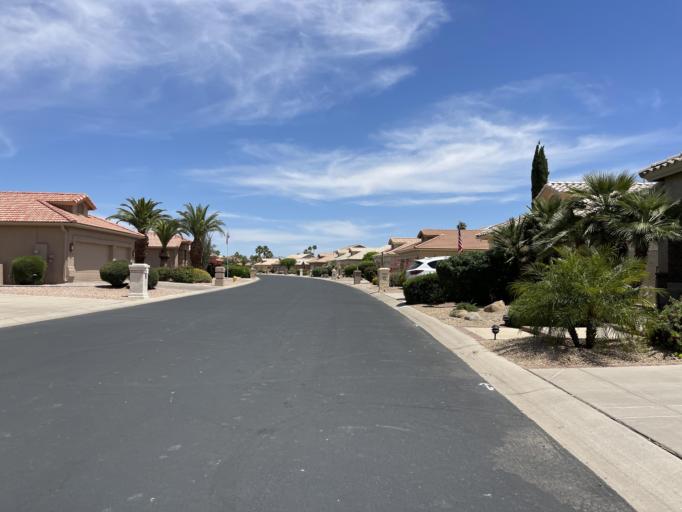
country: US
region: Arizona
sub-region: Maricopa County
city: Sun Lakes
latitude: 33.2278
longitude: -111.8788
